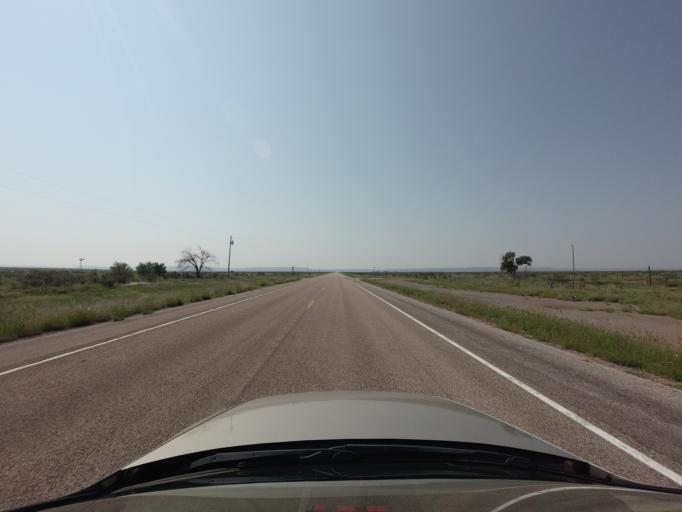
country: US
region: New Mexico
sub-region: Quay County
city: Tucumcari
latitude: 34.9244
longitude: -103.7602
